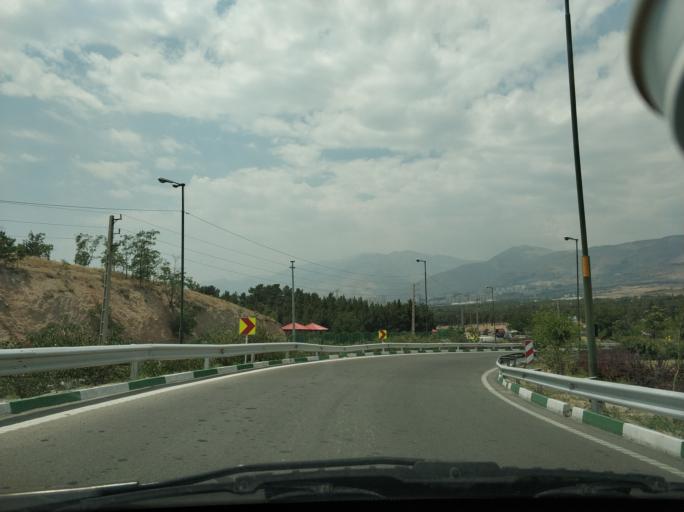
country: IR
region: Tehran
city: Tajrish
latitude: 35.7690
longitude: 51.5553
